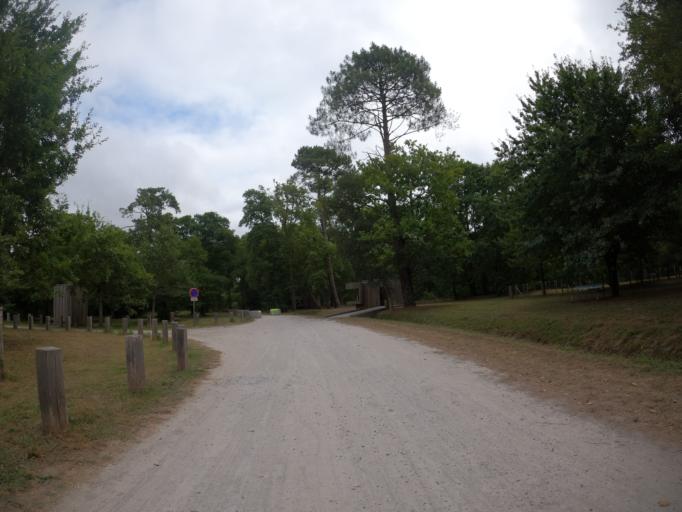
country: FR
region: Aquitaine
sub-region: Departement des Landes
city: Leon
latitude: 43.8872
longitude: -1.3150
